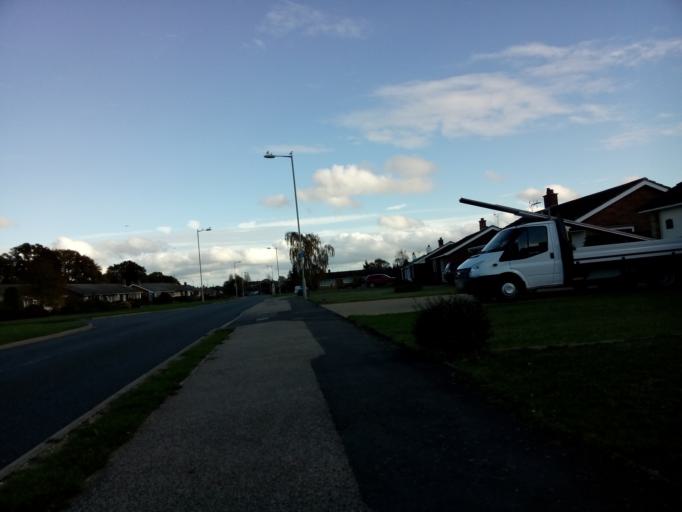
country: GB
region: England
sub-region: Suffolk
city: Kesgrave
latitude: 52.0580
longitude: 1.2220
